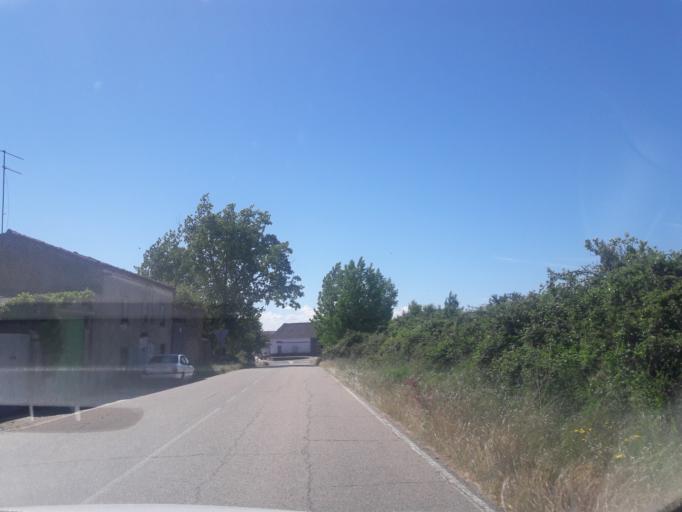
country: ES
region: Castille and Leon
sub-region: Provincia de Salamanca
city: Vitigudino
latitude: 41.0100
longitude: -6.4396
